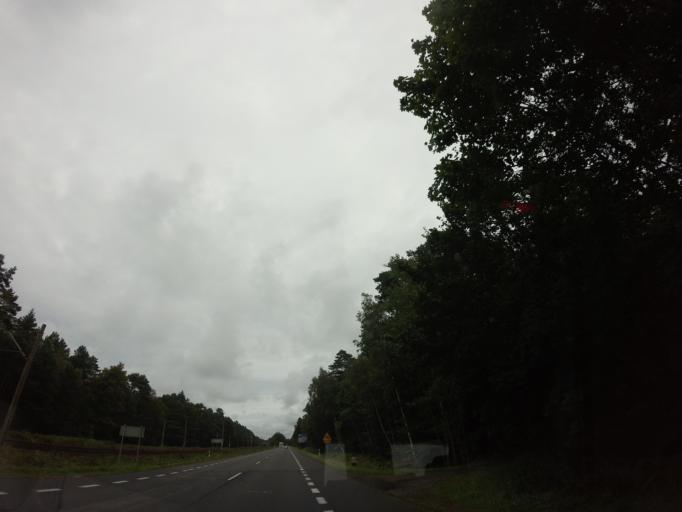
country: PL
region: West Pomeranian Voivodeship
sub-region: Powiat kamienski
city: Miedzyzdroje
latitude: 53.9098
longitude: 14.3960
